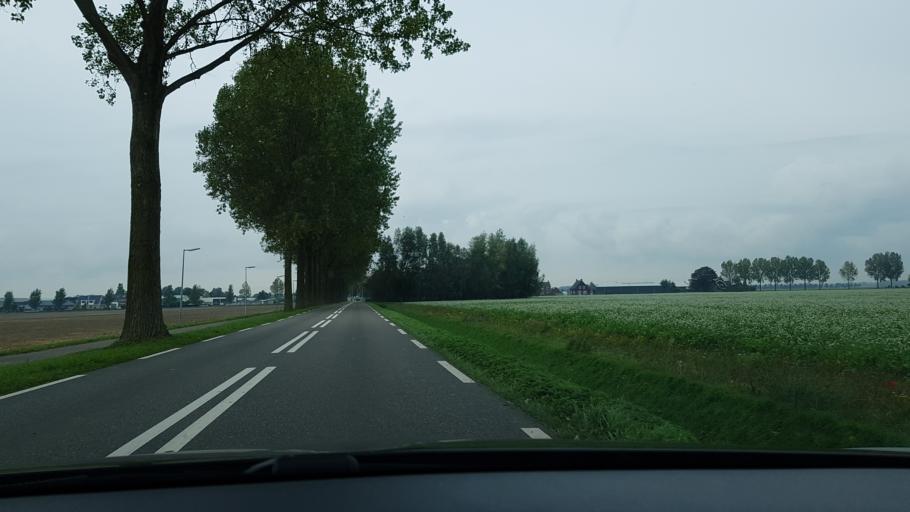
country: NL
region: South Holland
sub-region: Gemeente Kaag en Braassem
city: Leimuiden
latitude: 52.2499
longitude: 4.6618
